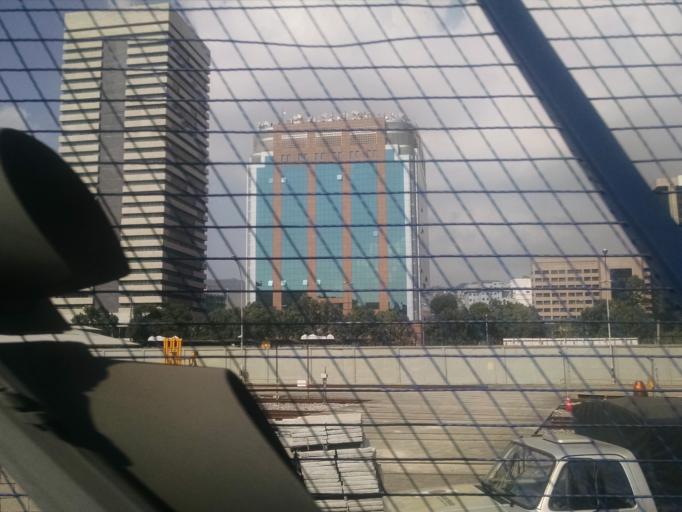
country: BR
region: Rio de Janeiro
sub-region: Rio De Janeiro
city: Rio de Janeiro
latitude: -22.9087
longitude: -43.2055
